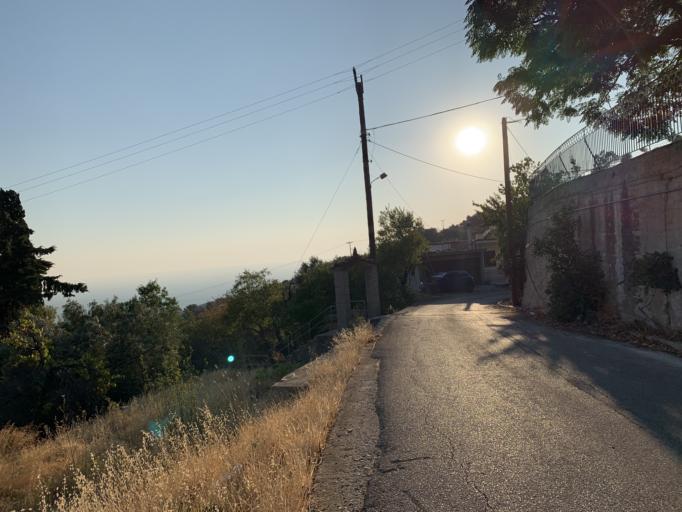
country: GR
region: North Aegean
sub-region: Chios
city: Vrontados
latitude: 38.5268
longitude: 25.8677
